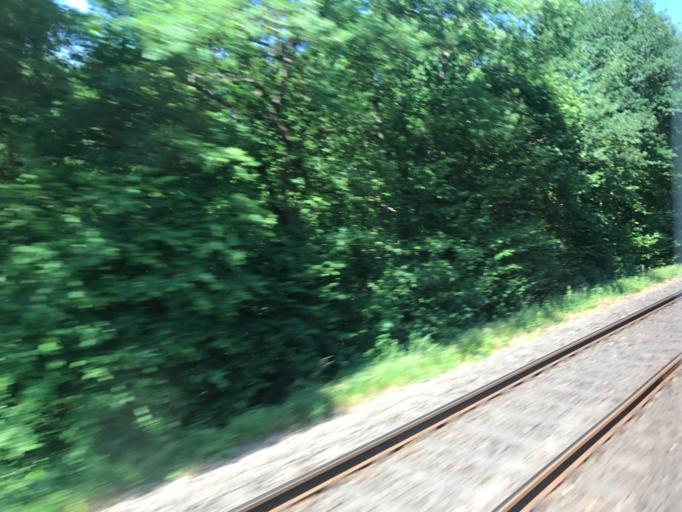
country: DE
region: Rheinland-Pfalz
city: Hoppstadten-Weiersbach
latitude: 49.6141
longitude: 7.2078
